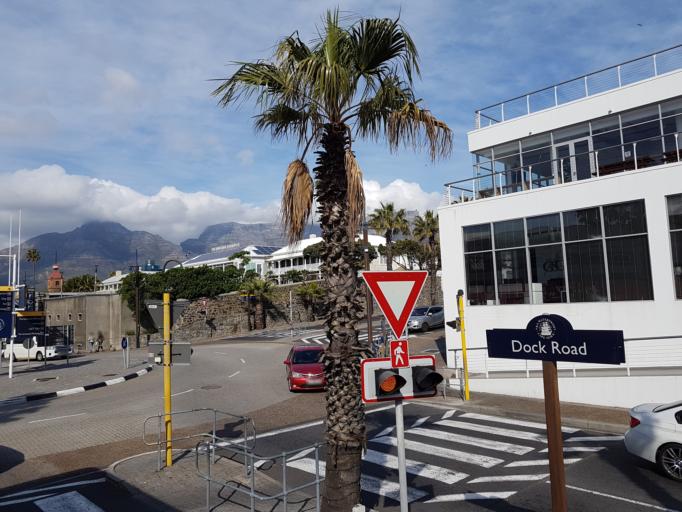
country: ZA
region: Western Cape
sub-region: City of Cape Town
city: Cape Town
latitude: -33.9046
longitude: 18.4185
